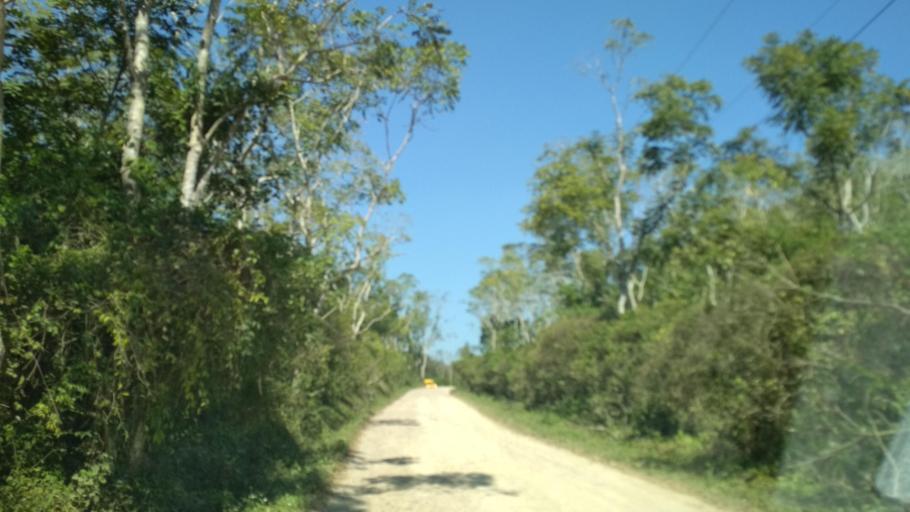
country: MX
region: Veracruz
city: Gutierrez Zamora
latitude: 20.4726
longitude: -97.1533
